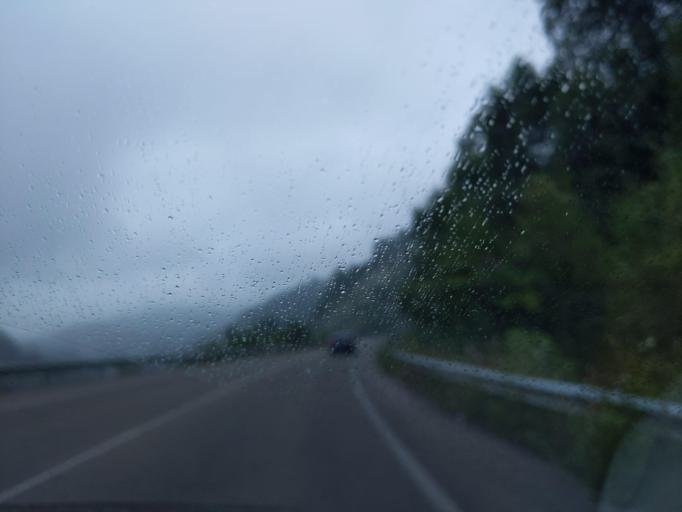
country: ES
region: Asturias
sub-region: Province of Asturias
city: El entrego
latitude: 43.2941
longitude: -5.6159
